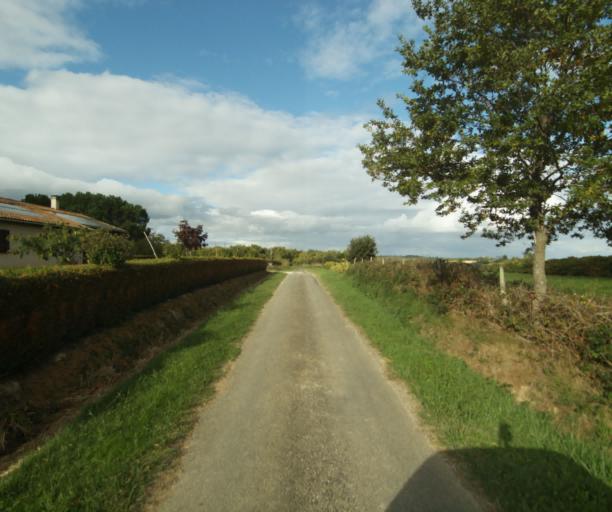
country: FR
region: Midi-Pyrenees
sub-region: Departement du Gers
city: Eauze
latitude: 43.8802
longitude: 0.0835
